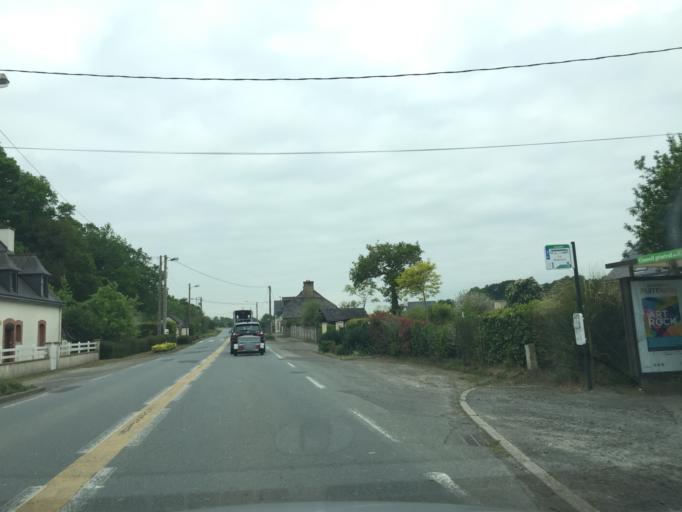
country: FR
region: Brittany
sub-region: Departement des Cotes-d'Armor
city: Lamballe
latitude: 48.5019
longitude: -2.4647
